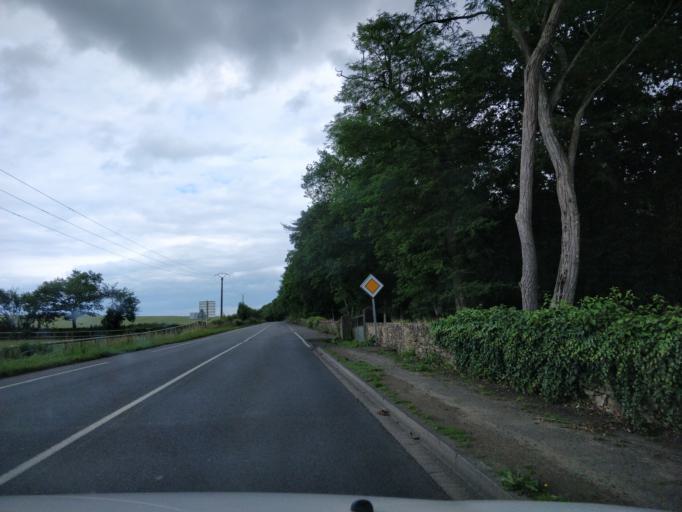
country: FR
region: Pays de la Loire
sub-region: Departement de Maine-et-Loire
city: Grez-Neuville
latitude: 47.6314
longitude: -0.7034
